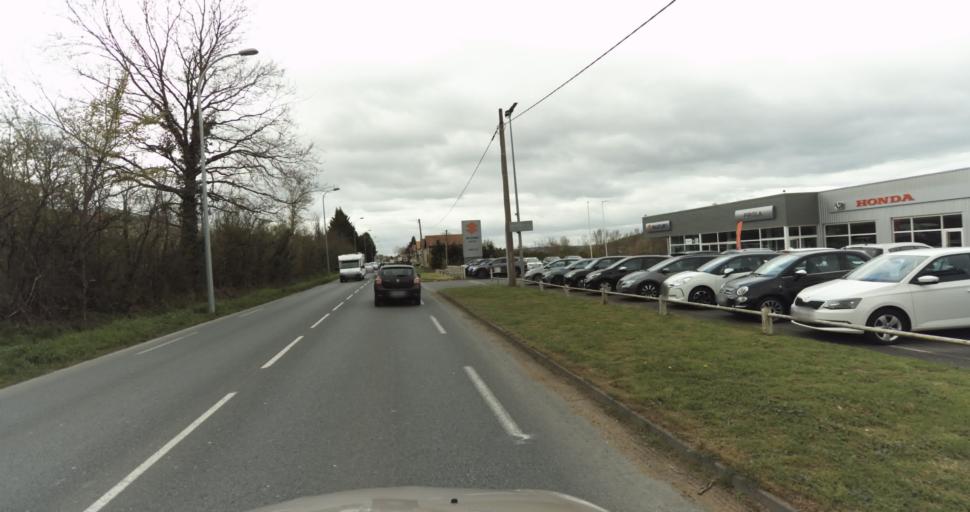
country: FR
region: Midi-Pyrenees
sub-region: Departement du Tarn
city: Puygouzon
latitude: 43.9005
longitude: 2.1472
